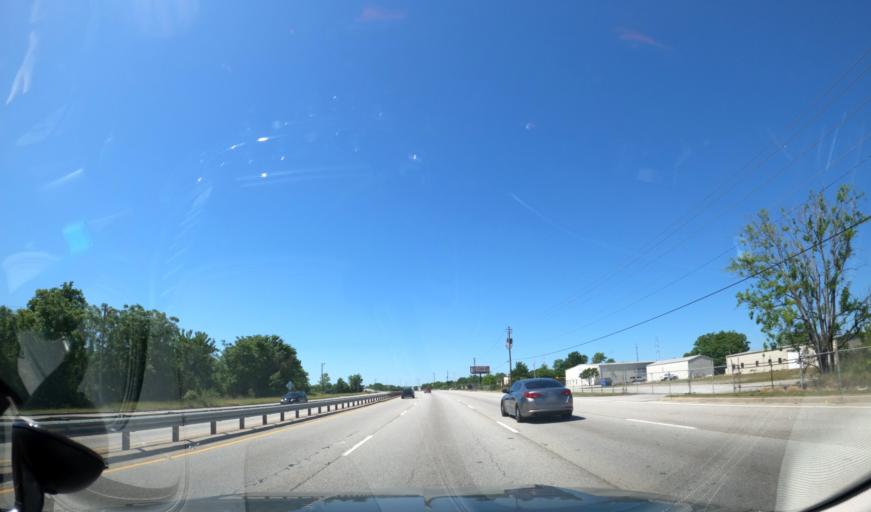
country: US
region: Georgia
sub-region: Richmond County
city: Augusta
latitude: 33.4535
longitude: -81.9715
